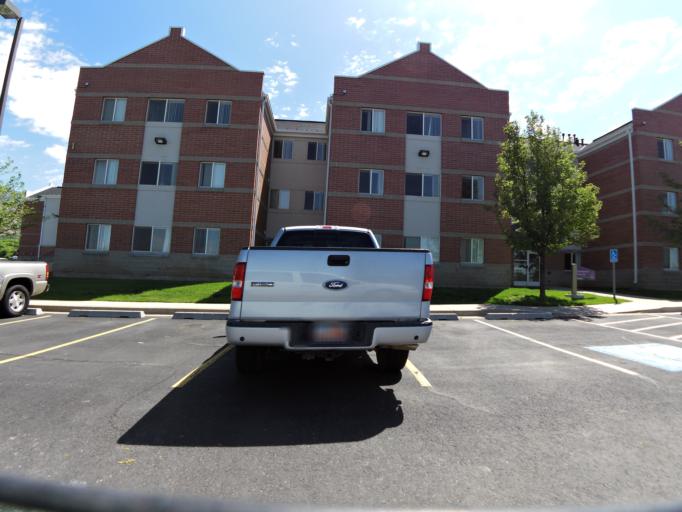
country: US
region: Utah
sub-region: Weber County
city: South Ogden
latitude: 41.1787
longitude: -111.9475
